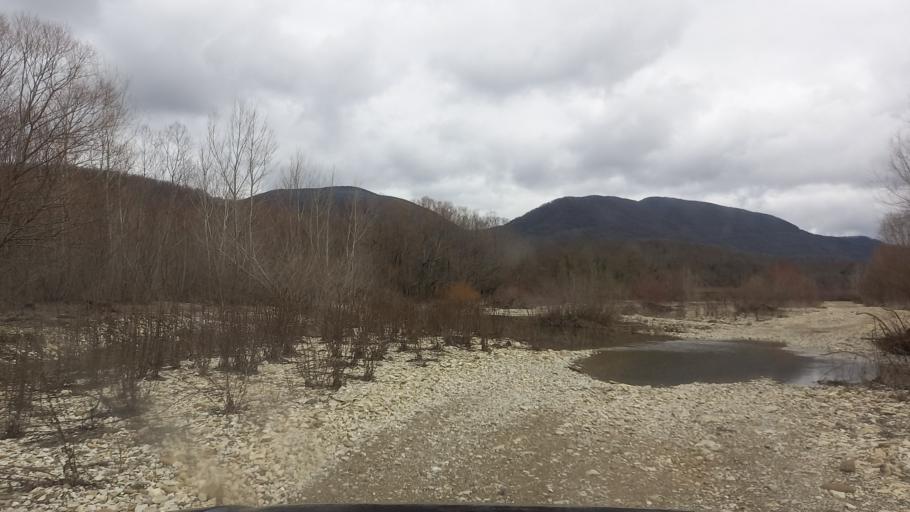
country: RU
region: Krasnodarskiy
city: Pshada
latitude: 44.4889
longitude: 38.4120
